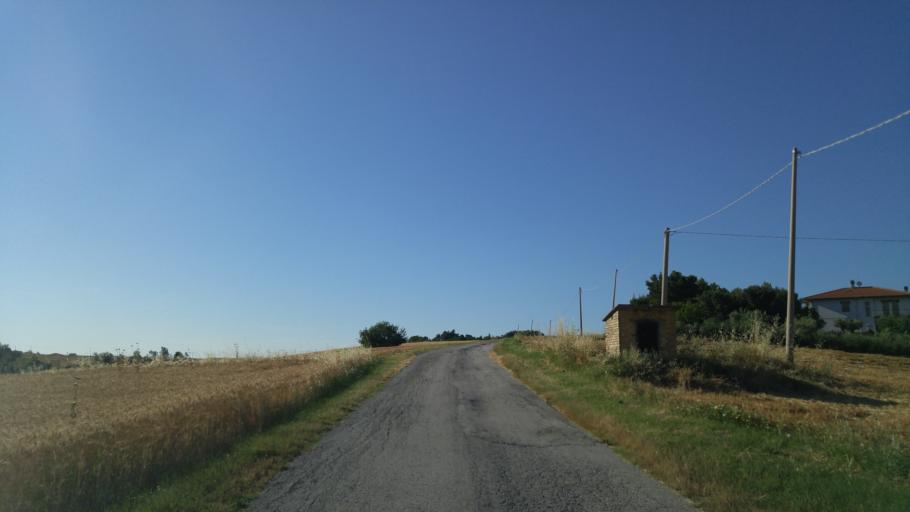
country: IT
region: The Marches
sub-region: Provincia di Pesaro e Urbino
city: Cartoceto
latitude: 43.7936
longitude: 12.8853
